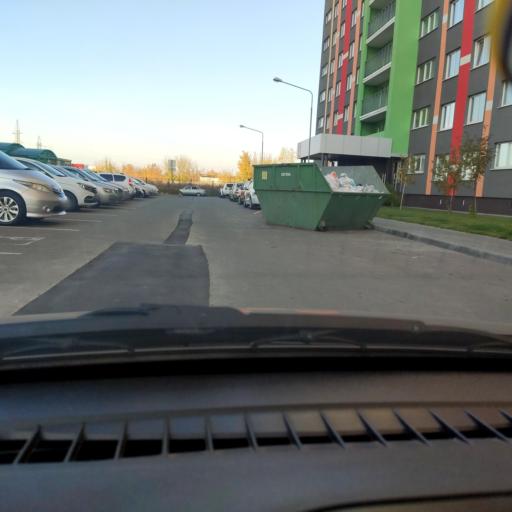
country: RU
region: Samara
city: Tol'yatti
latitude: 53.5185
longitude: 49.2564
